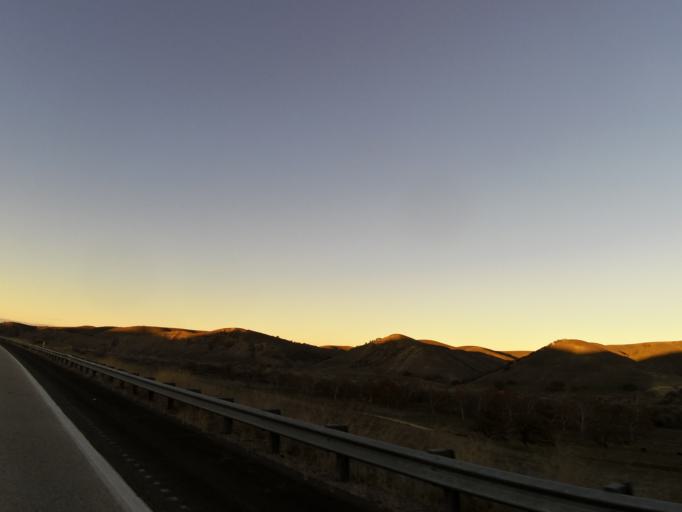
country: US
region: California
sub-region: San Luis Obispo County
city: Lake Nacimiento
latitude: 35.9034
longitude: -120.8426
